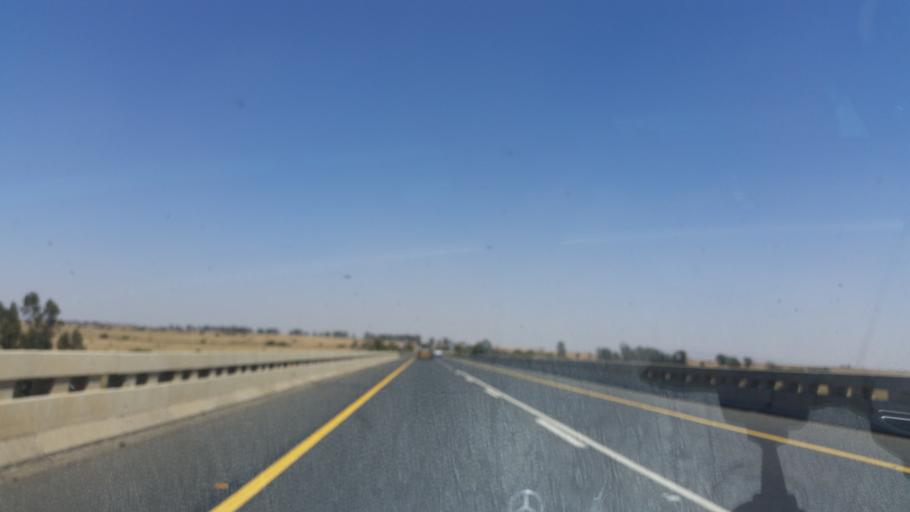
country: ZA
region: Orange Free State
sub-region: Lejweleputswa District Municipality
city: Winburg
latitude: -28.6315
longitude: 26.9038
